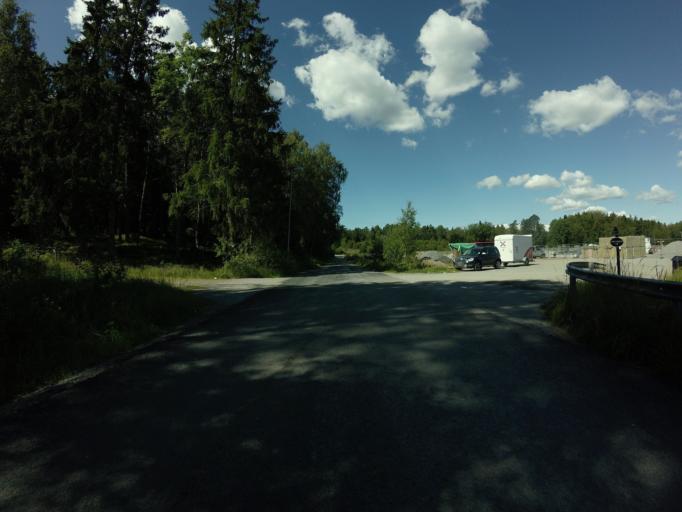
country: SE
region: Stockholm
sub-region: Jarfalla Kommun
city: Jakobsberg
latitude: 59.4631
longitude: 17.8810
